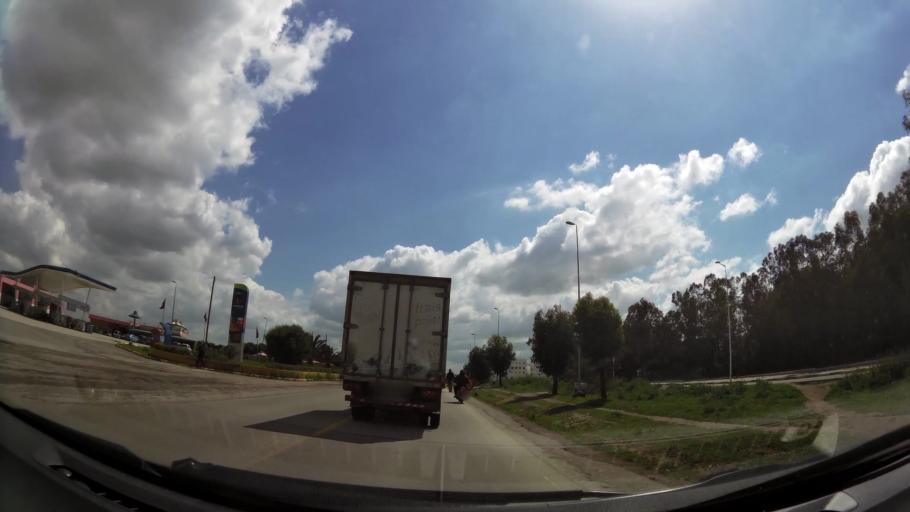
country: MA
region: Chaouia-Ouardigha
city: Nouaseur
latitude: 33.3693
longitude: -7.5431
